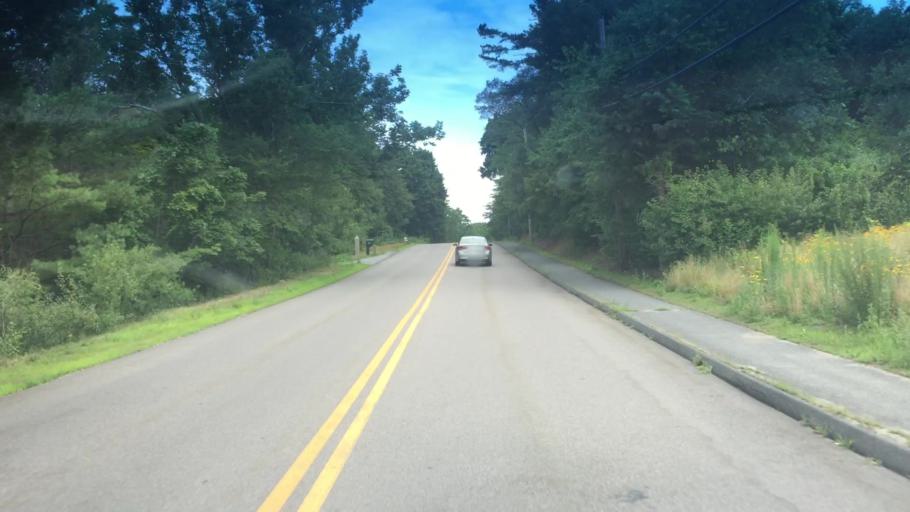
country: US
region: Massachusetts
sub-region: Norfolk County
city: Medway
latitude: 42.1192
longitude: -71.3966
